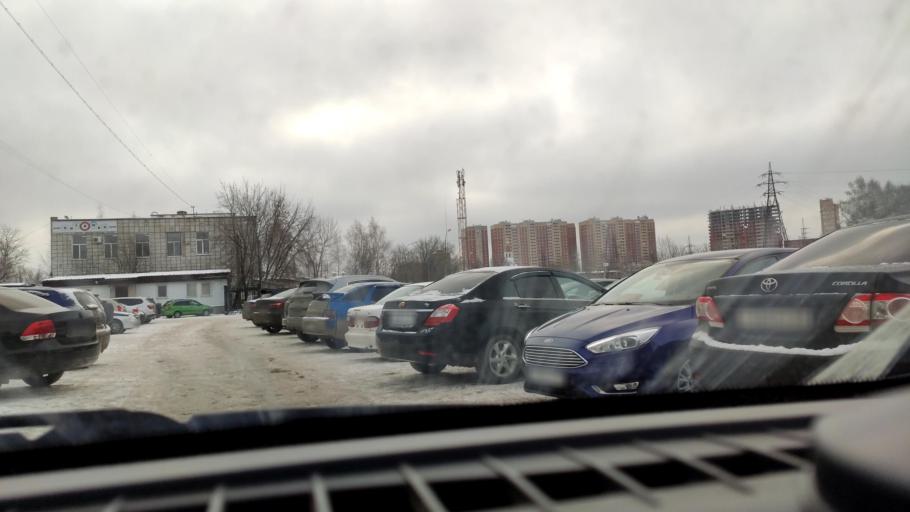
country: RU
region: Perm
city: Perm
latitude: 57.9923
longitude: 56.2907
